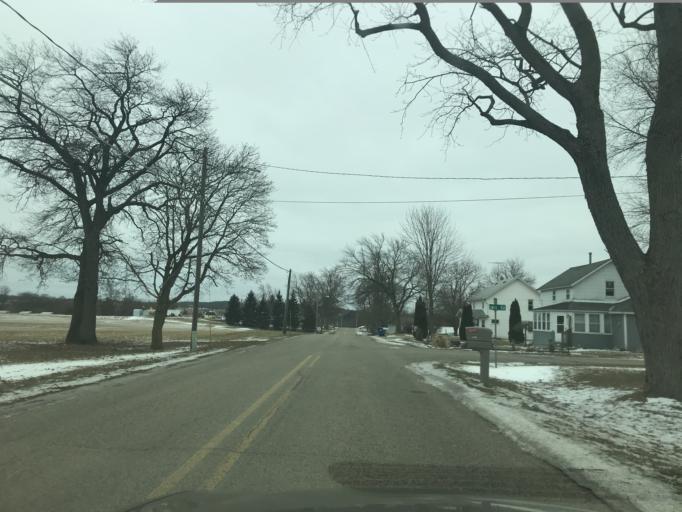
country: US
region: Michigan
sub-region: Jackson County
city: Brooklyn
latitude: 42.0672
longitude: -84.3260
